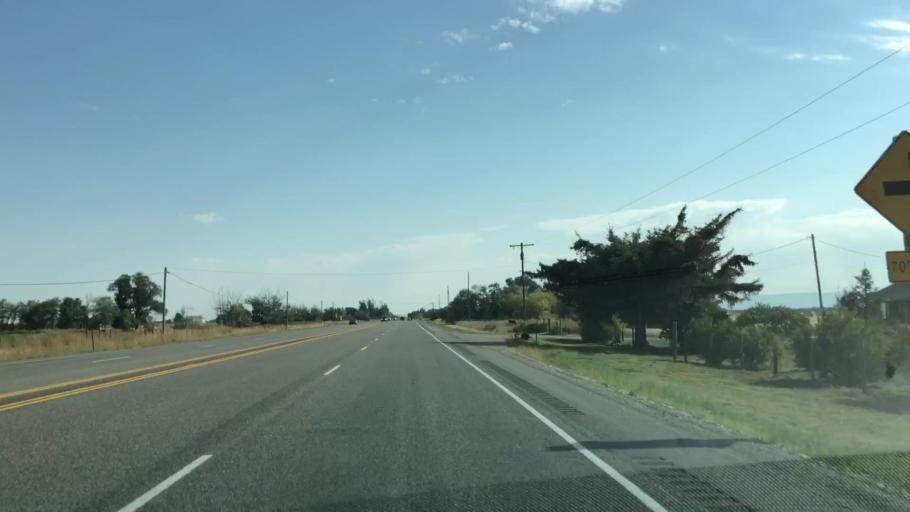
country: US
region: Idaho
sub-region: Bonneville County
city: Iona
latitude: 43.5772
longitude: -111.9043
